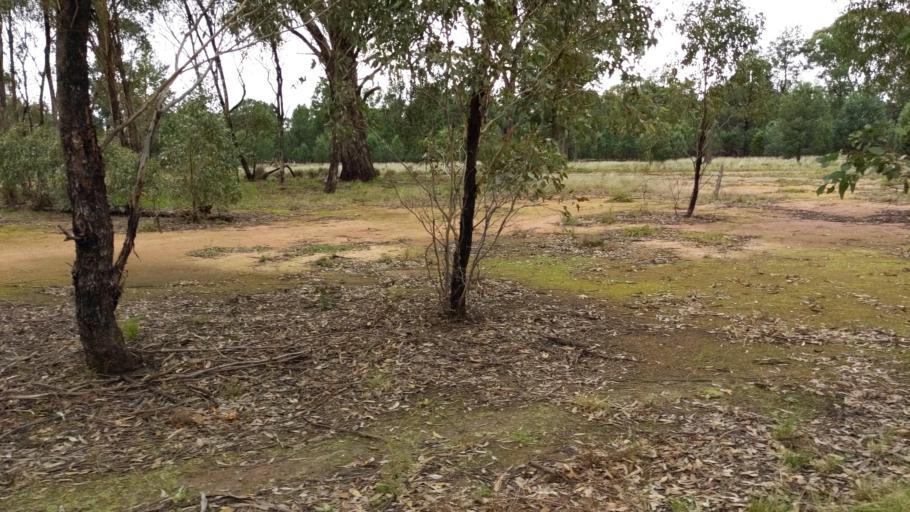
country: AU
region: New South Wales
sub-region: Coolamon
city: Coolamon
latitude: -34.8606
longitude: 146.9216
